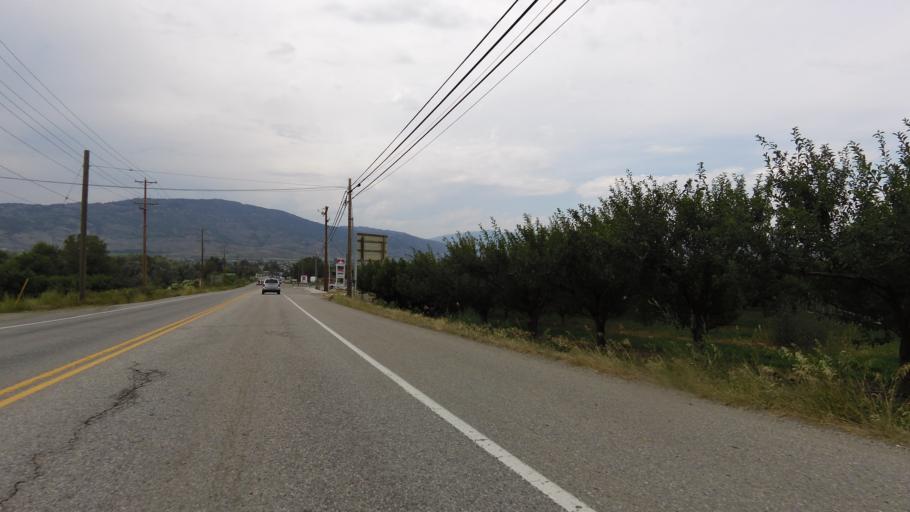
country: CA
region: British Columbia
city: Osoyoos
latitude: 49.0279
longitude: -119.4346
